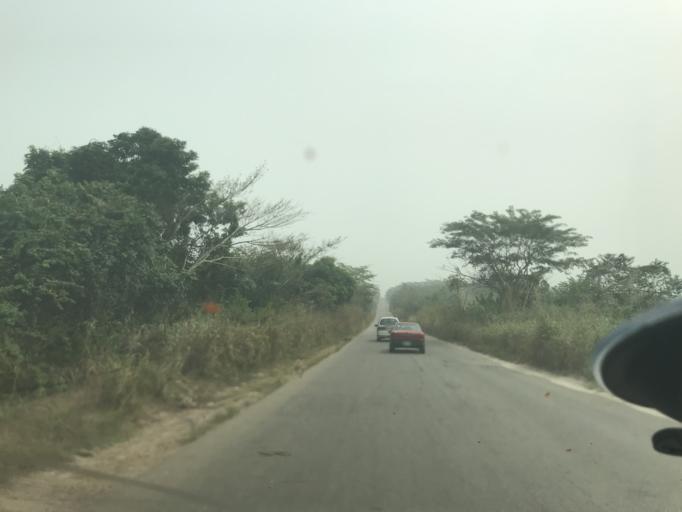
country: NG
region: Ogun
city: Ilaro
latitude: 6.8859
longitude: 3.0679
